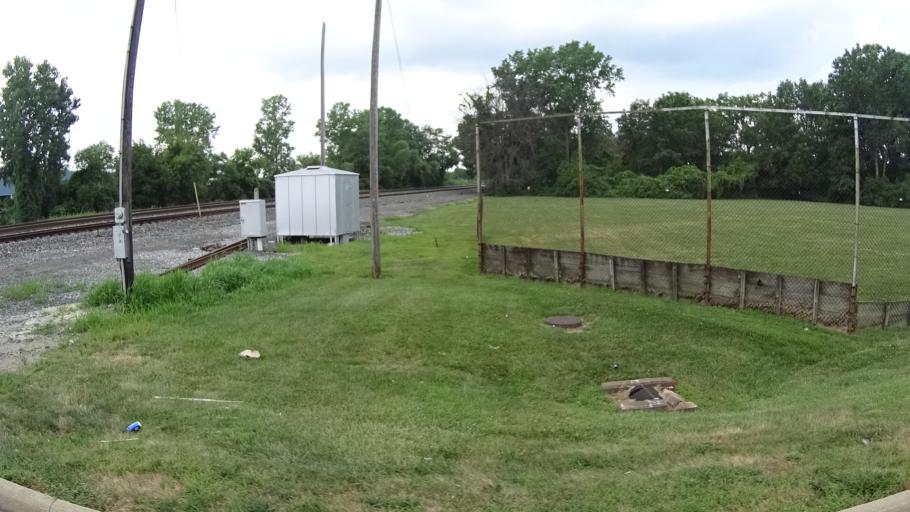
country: US
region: Ohio
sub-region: Erie County
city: Sandusky
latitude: 41.4439
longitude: -82.7515
